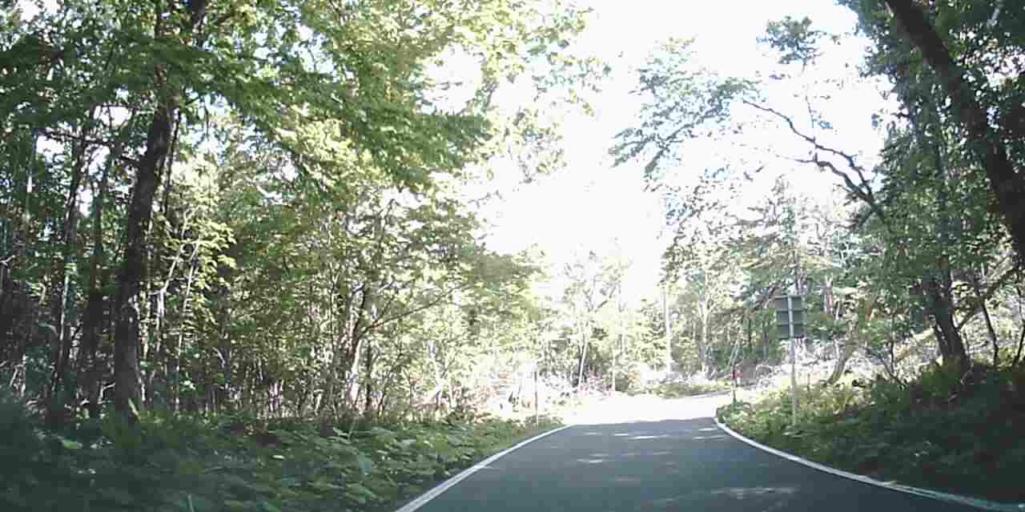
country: JP
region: Hokkaido
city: Shiraoi
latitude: 42.7299
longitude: 141.4134
